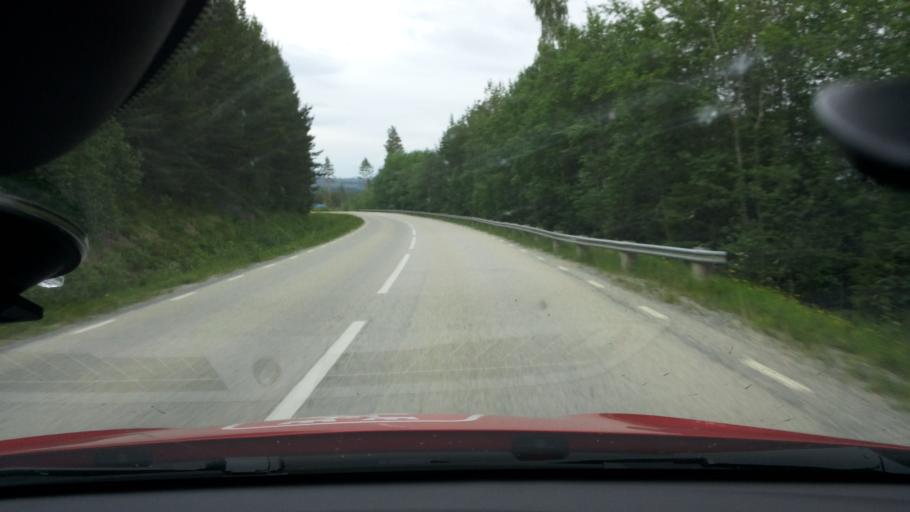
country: SE
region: Jaemtland
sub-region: Bergs Kommun
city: Hoverberg
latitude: 62.6387
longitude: 14.3570
